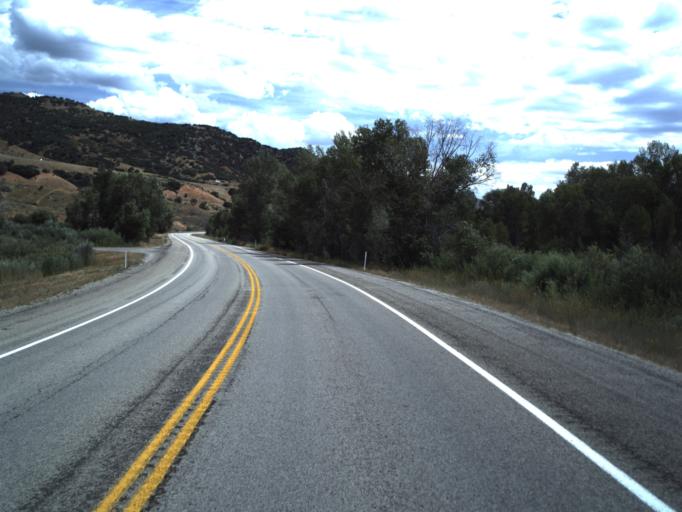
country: US
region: Utah
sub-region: Utah County
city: Woodland Hills
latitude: 39.9942
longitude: -111.4922
